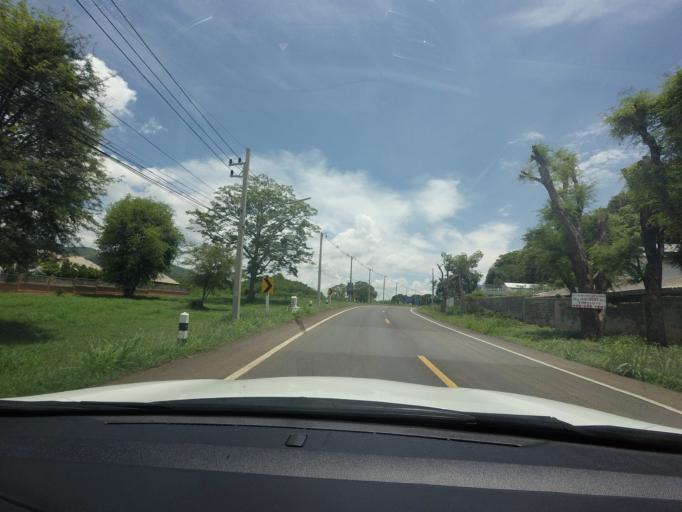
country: TH
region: Sara Buri
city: Muak Lek
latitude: 14.5858
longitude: 101.2448
